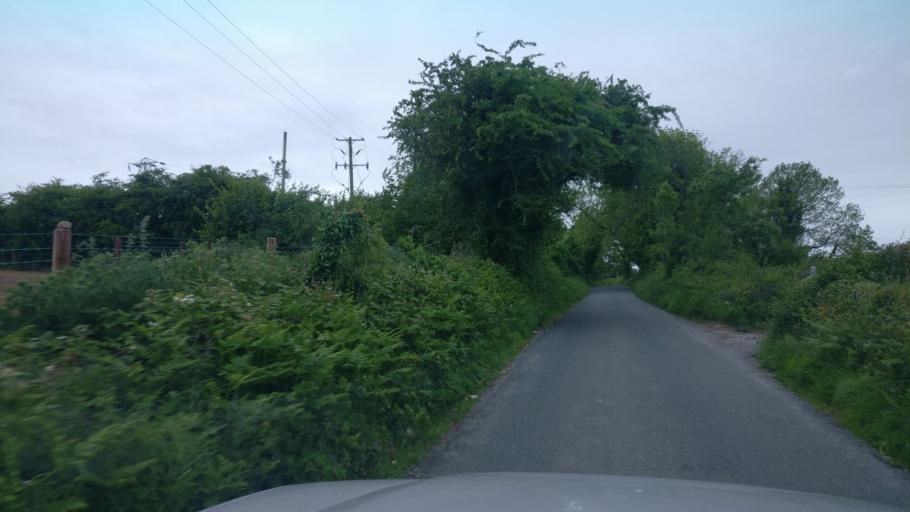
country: IE
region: Connaught
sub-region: County Galway
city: Loughrea
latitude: 53.1212
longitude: -8.4379
